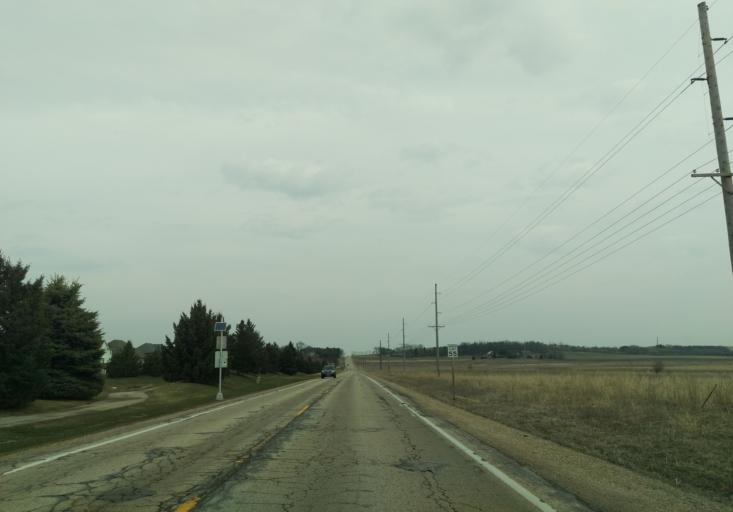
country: US
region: Wisconsin
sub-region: Dane County
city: Waunakee
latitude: 43.2033
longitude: -89.4616
